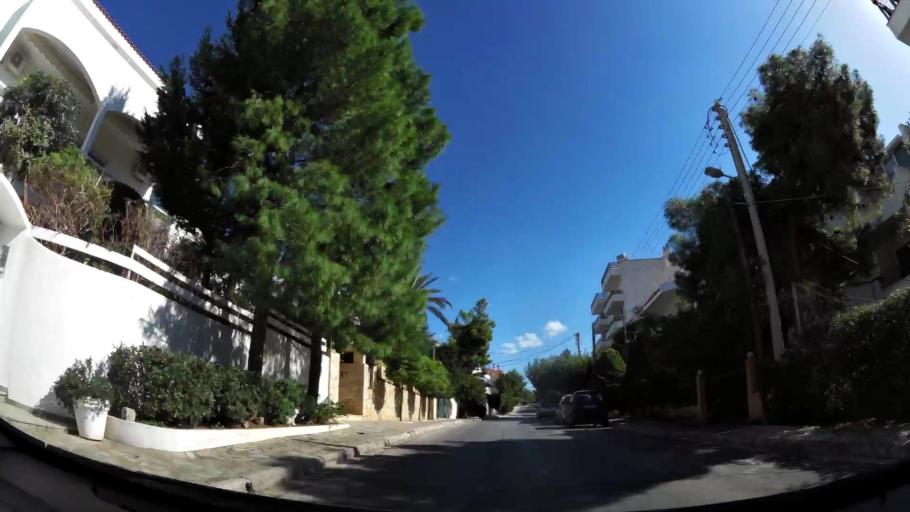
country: GR
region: Attica
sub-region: Nomarchia Anatolikis Attikis
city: Voula
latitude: 37.8472
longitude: 23.7735
